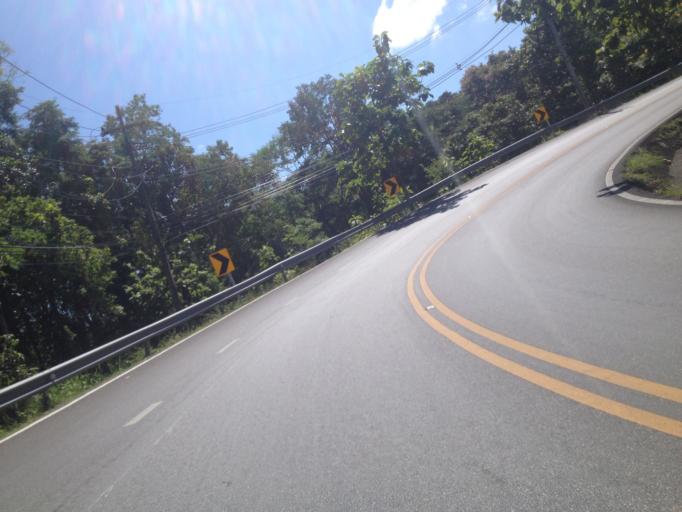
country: TH
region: Chiang Mai
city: Chiang Mai
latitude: 18.8116
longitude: 98.9385
